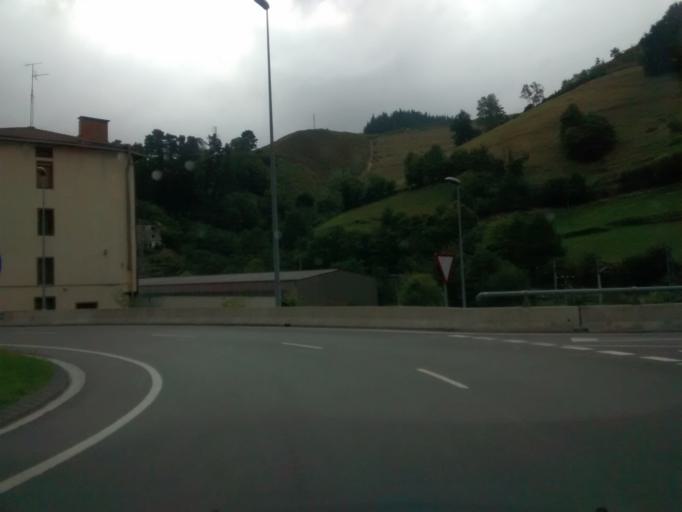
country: ES
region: Basque Country
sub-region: Bizkaia
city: Ermua
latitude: 43.1779
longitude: -2.4941
